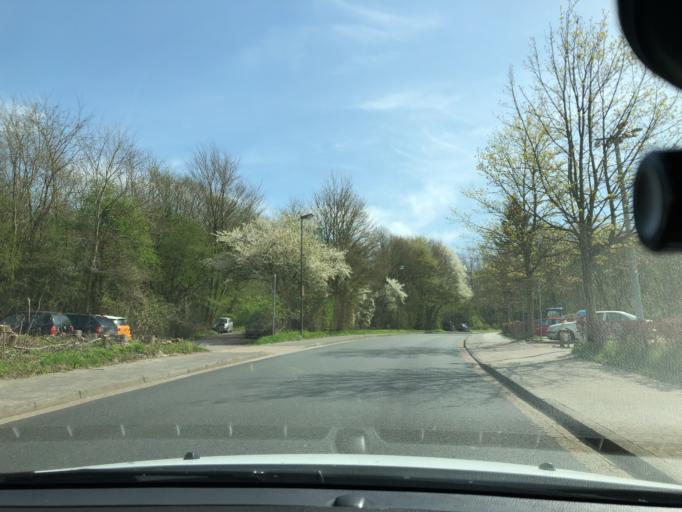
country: DE
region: Schleswig-Holstein
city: Flensburg
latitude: 54.7748
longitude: 9.4459
